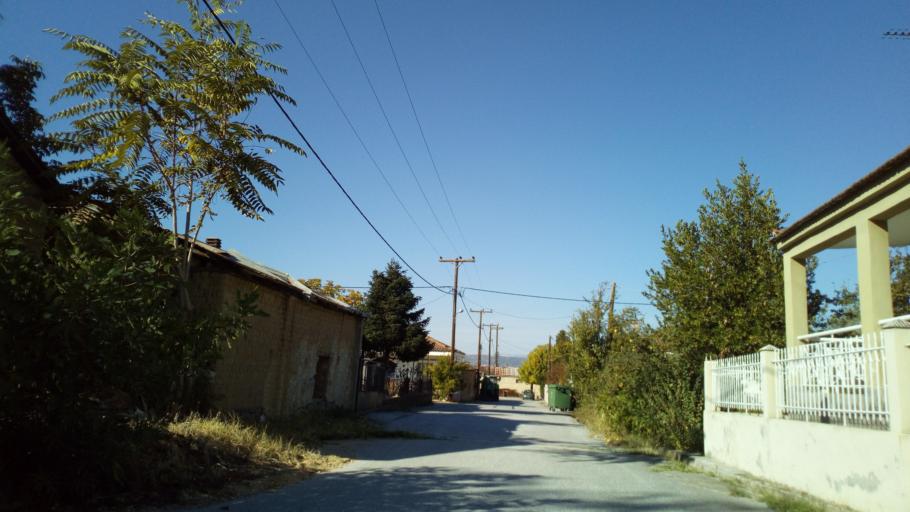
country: GR
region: Central Macedonia
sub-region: Nomos Thessalonikis
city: Gerakarou
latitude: 40.6345
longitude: 23.2492
